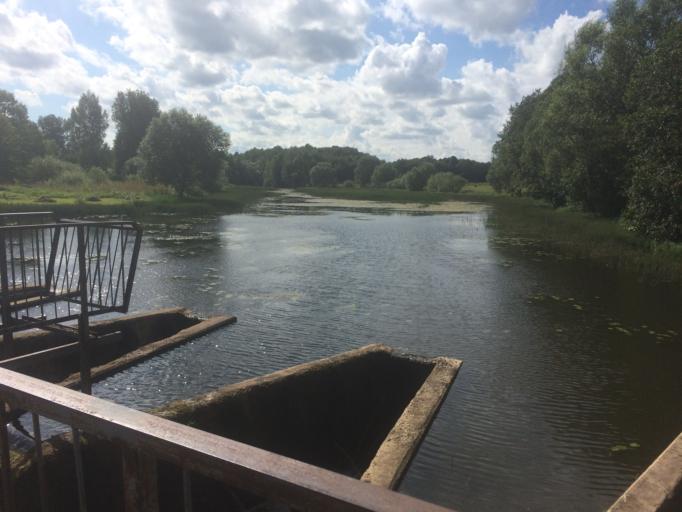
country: LV
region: Karsava
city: Karsava
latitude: 56.7137
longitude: 27.7410
